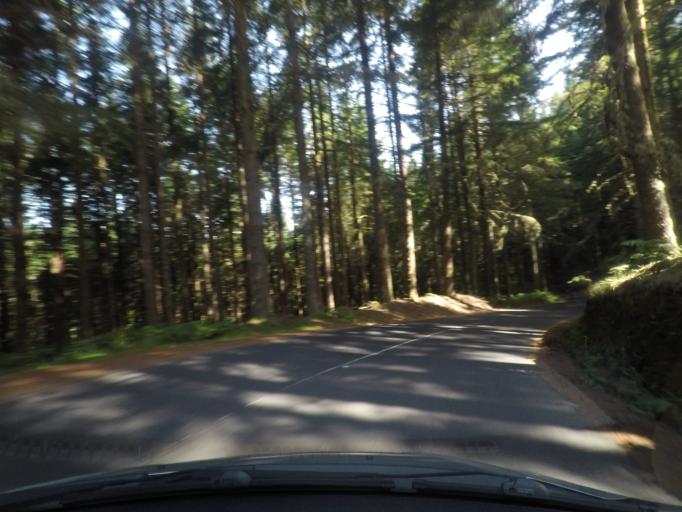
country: PT
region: Madeira
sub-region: Funchal
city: Nossa Senhora do Monte
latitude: 32.7194
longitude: -16.8884
